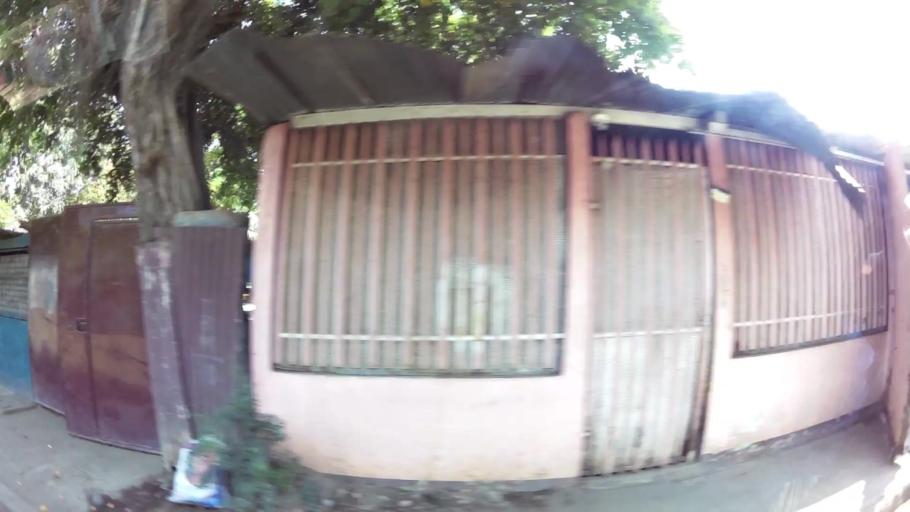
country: NI
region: Managua
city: Ciudad Sandino
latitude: 12.1598
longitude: -86.3114
